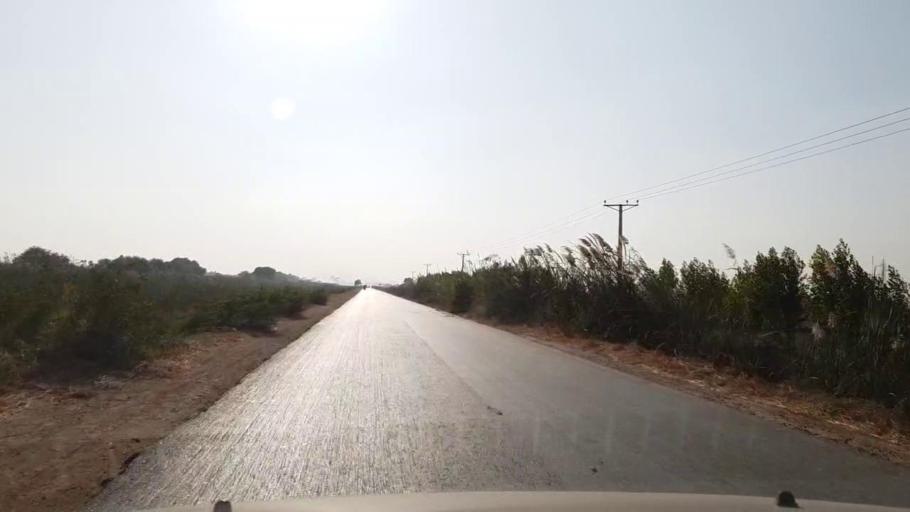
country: PK
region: Sindh
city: Tando Muhammad Khan
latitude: 25.0469
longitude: 68.4451
